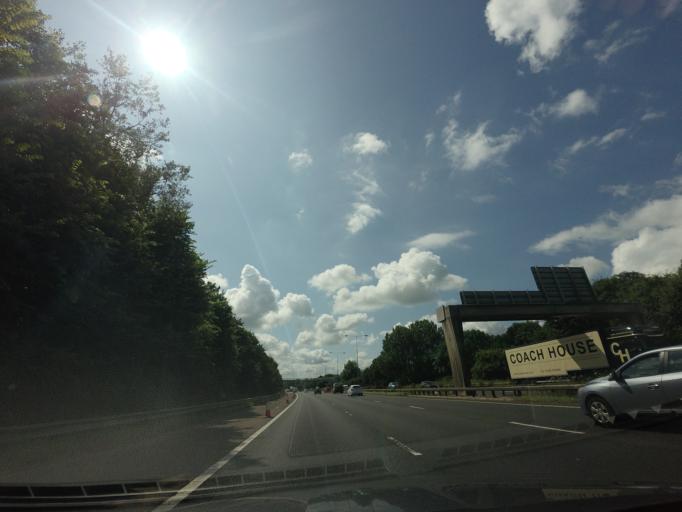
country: GB
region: England
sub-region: Lancashire
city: Clayton-le-Woods
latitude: 53.7059
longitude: -2.6760
